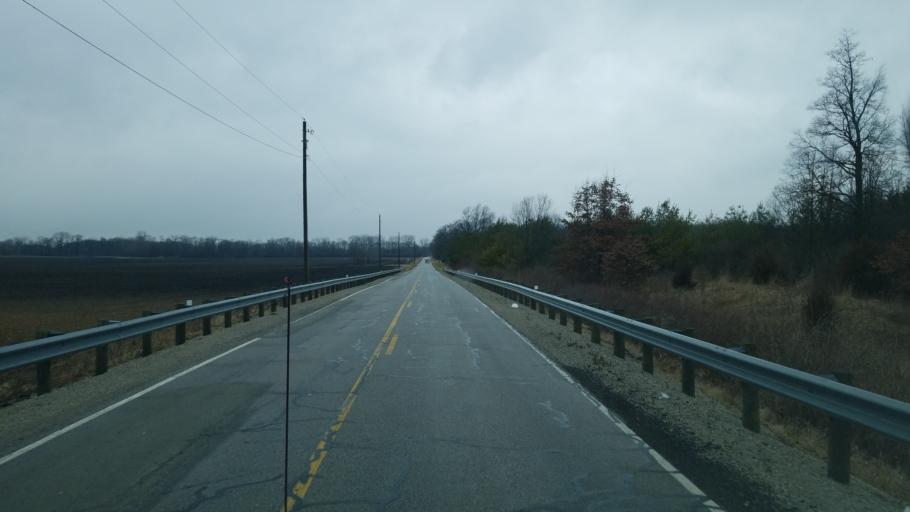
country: US
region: Ohio
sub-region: Marion County
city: Marion
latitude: 40.6206
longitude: -83.1642
